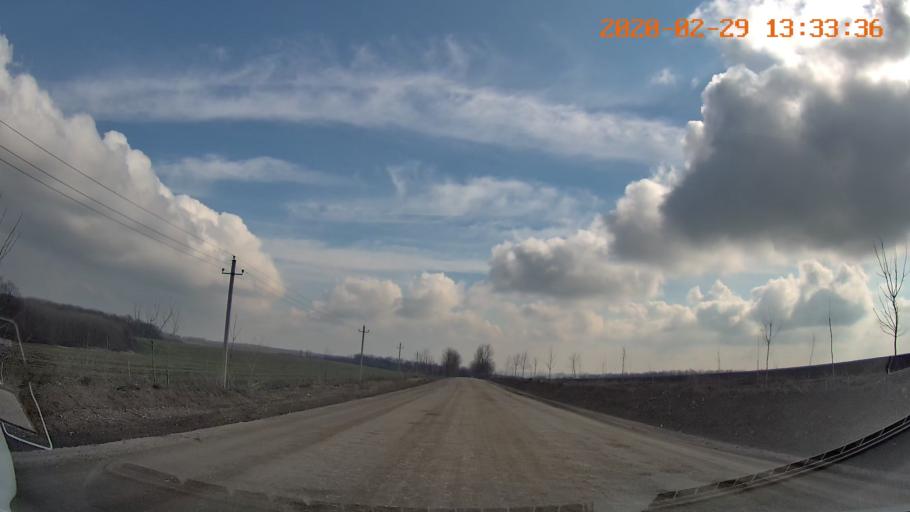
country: MD
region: Telenesti
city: Camenca
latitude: 47.8727
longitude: 28.6176
